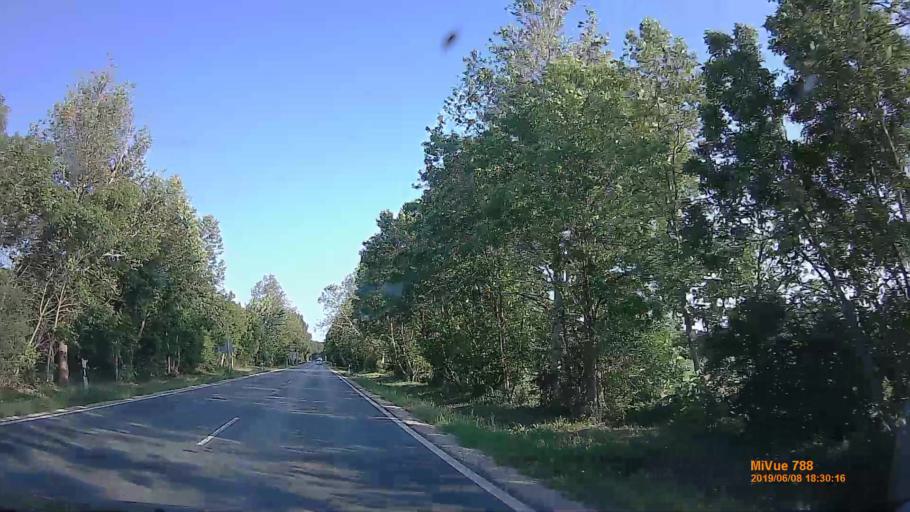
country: HU
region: Vas
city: Sarvar
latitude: 47.3763
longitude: 16.8837
